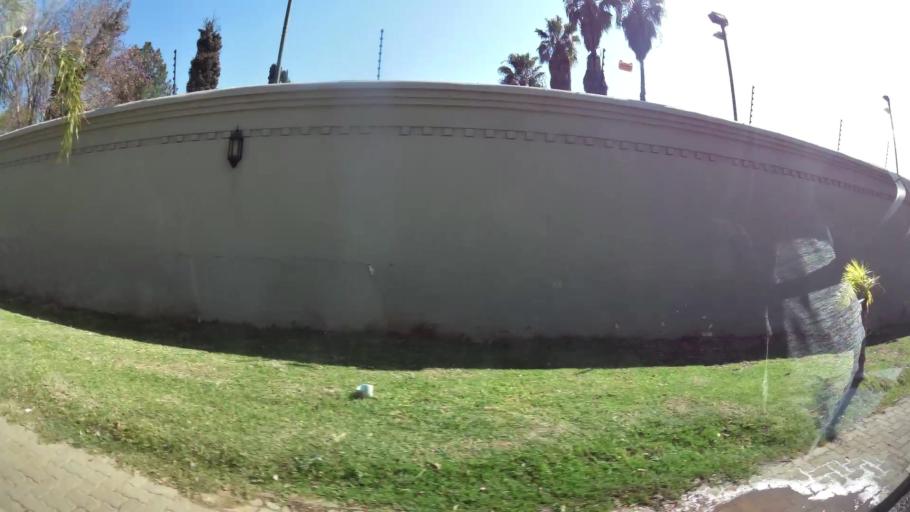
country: ZA
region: Gauteng
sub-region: City of Johannesburg Metropolitan Municipality
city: Johannesburg
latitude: -26.1092
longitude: 28.0422
